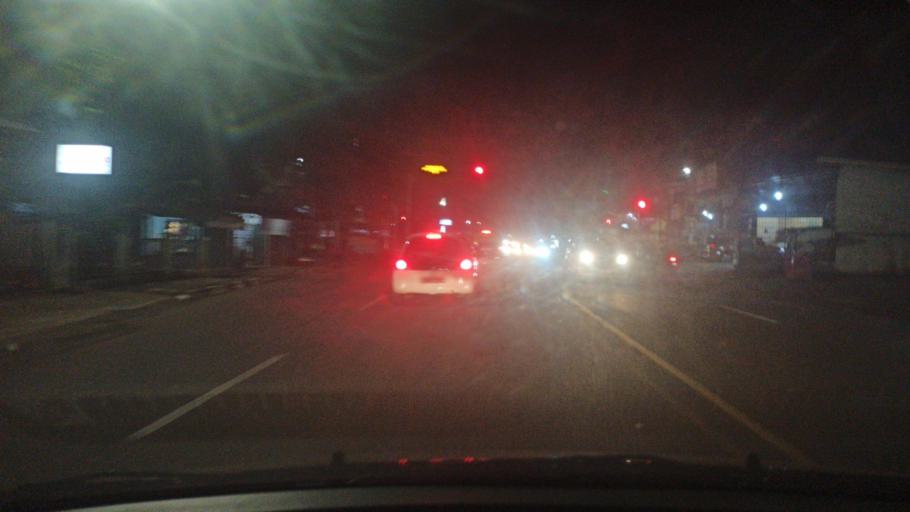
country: ID
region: South Sumatra
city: Palembang
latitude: -2.9875
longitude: 104.7252
